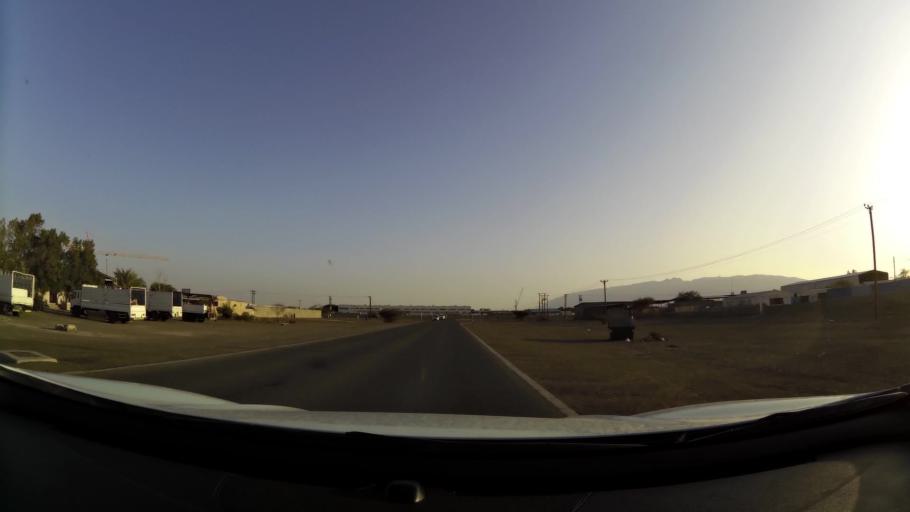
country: AE
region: Abu Dhabi
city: Al Ain
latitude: 24.1520
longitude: 55.8244
